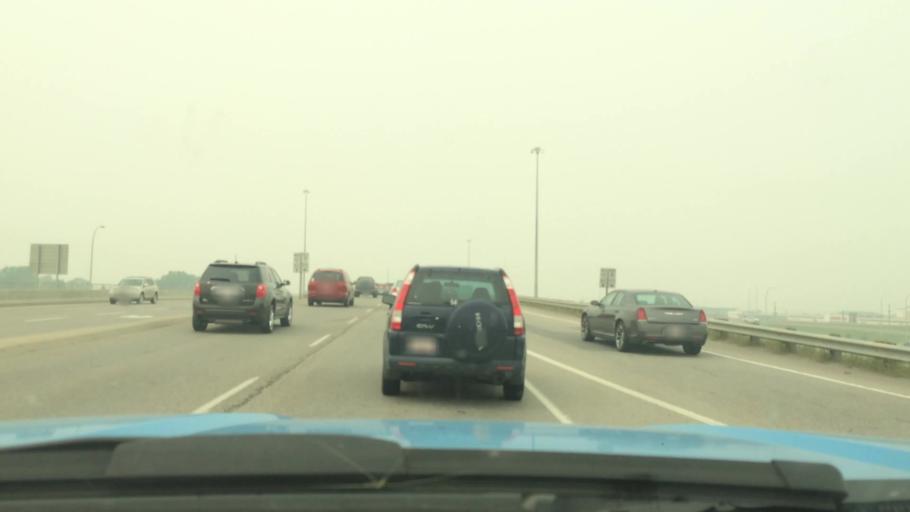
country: CA
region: Alberta
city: Airdrie
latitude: 51.3000
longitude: -113.9998
